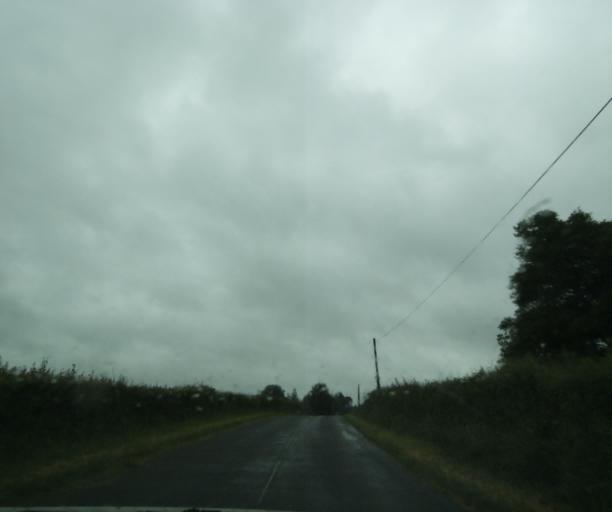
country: FR
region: Bourgogne
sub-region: Departement de Saone-et-Loire
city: Palinges
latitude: 46.5244
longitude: 4.2128
